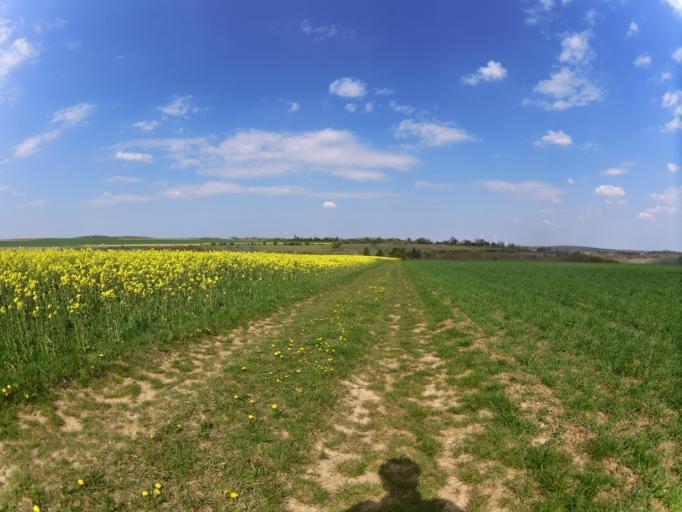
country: DE
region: Bavaria
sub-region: Regierungsbezirk Unterfranken
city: Winterhausen
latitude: 49.6844
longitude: 10.0130
